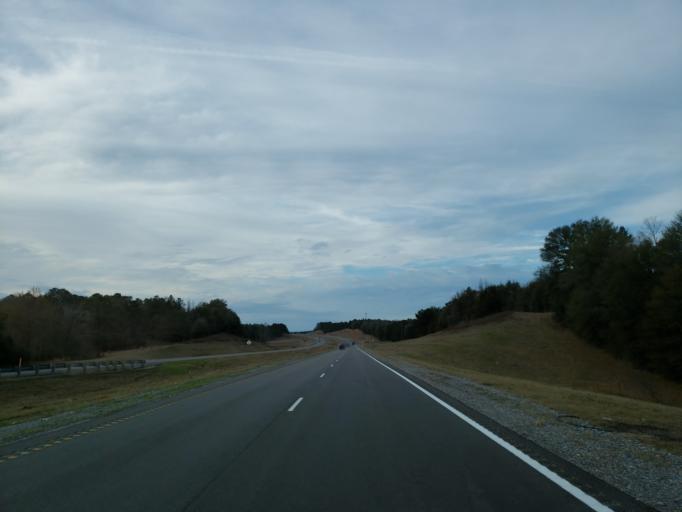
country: US
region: Mississippi
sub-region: Clarke County
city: Quitman
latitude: 32.0976
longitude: -88.7040
